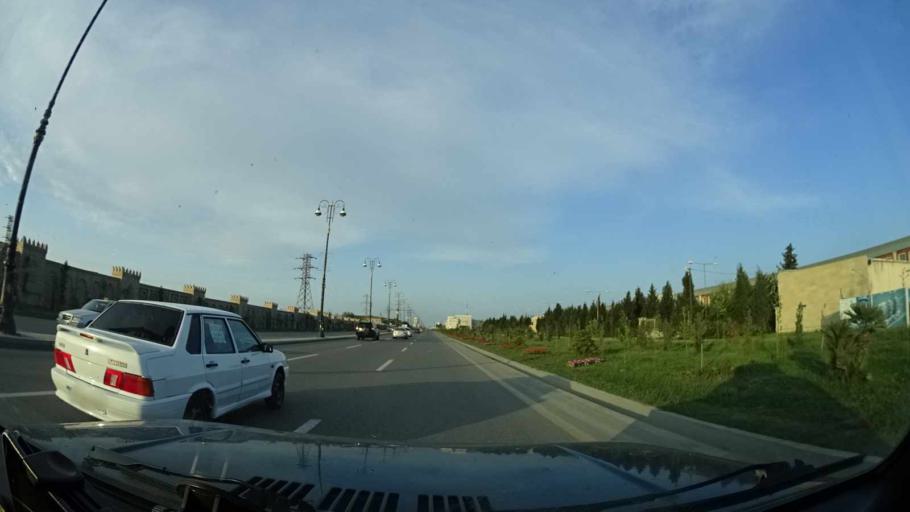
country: AZ
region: Sumqayit
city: Sumqayit
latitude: 40.5761
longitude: 49.6447
